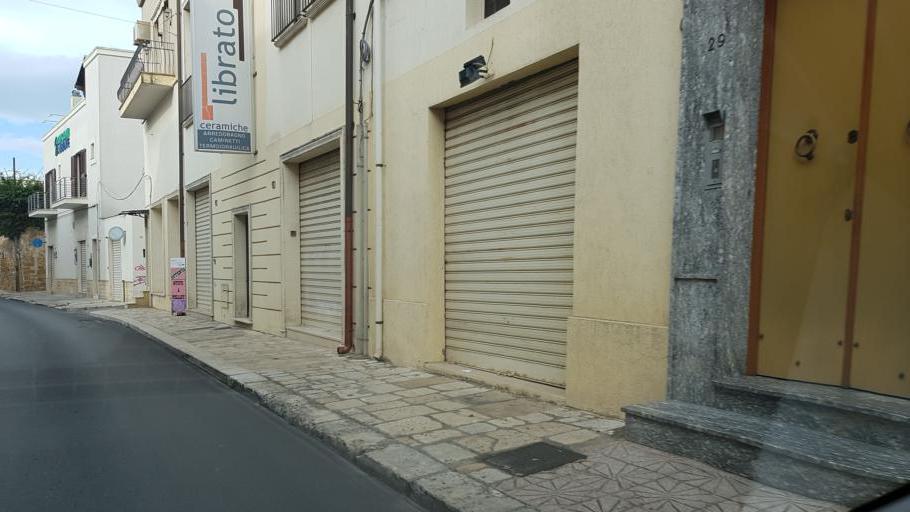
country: IT
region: Apulia
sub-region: Provincia di Brindisi
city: Mesagne
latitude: 40.5600
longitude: 17.8107
